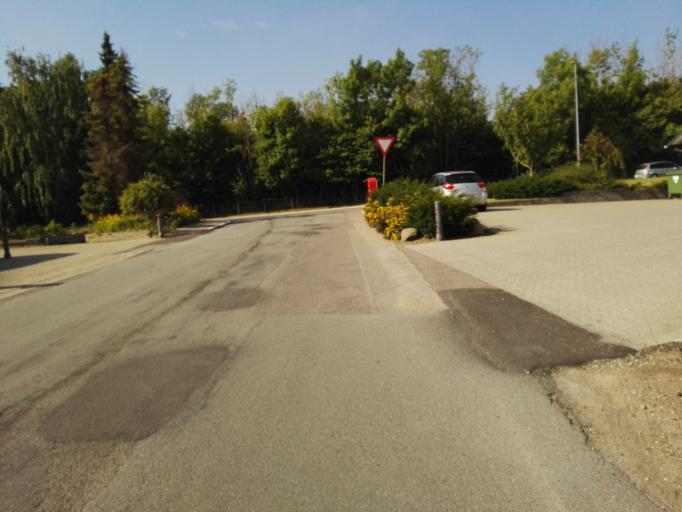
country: DK
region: Capital Region
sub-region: Egedal Kommune
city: Stenlose
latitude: 55.7722
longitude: 12.1987
